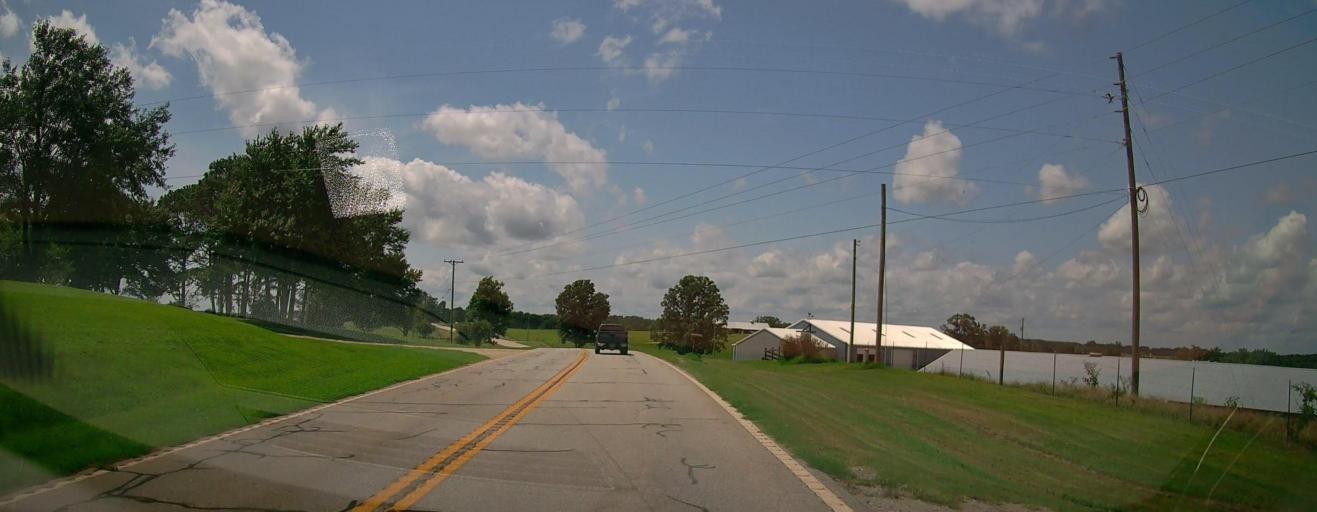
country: US
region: Georgia
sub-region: Heard County
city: Franklin
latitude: 33.3652
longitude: -85.2260
